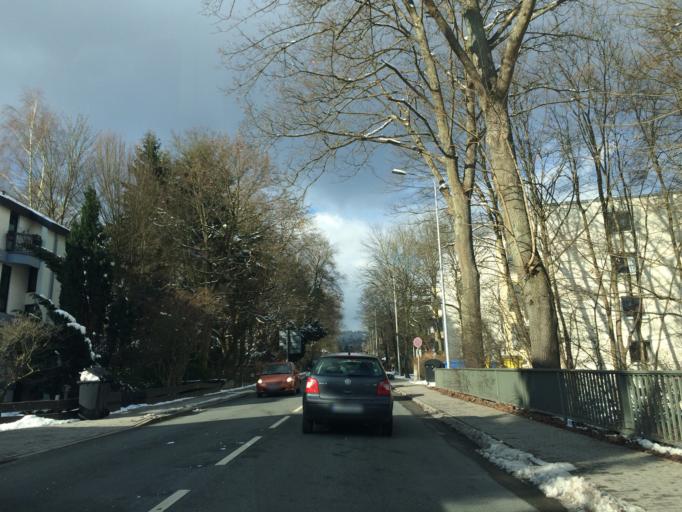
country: DE
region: Hesse
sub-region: Regierungsbezirk Darmstadt
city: Konigstein im Taunus
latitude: 50.1892
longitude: 8.4658
